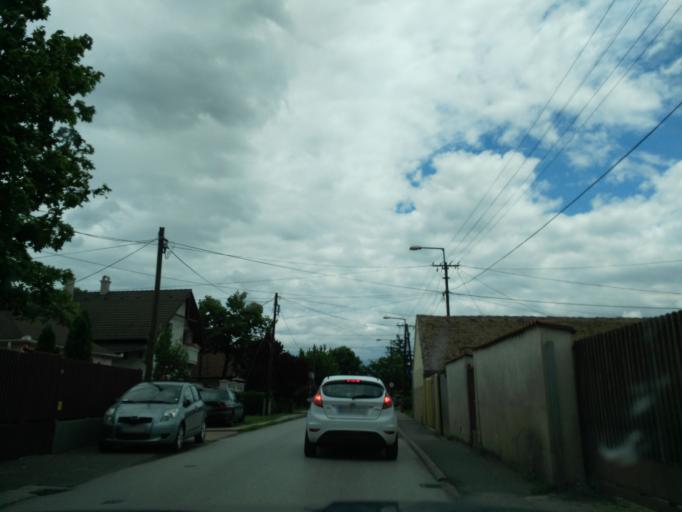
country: HU
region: Hajdu-Bihar
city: Debrecen
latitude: 47.5418
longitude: 21.6450
